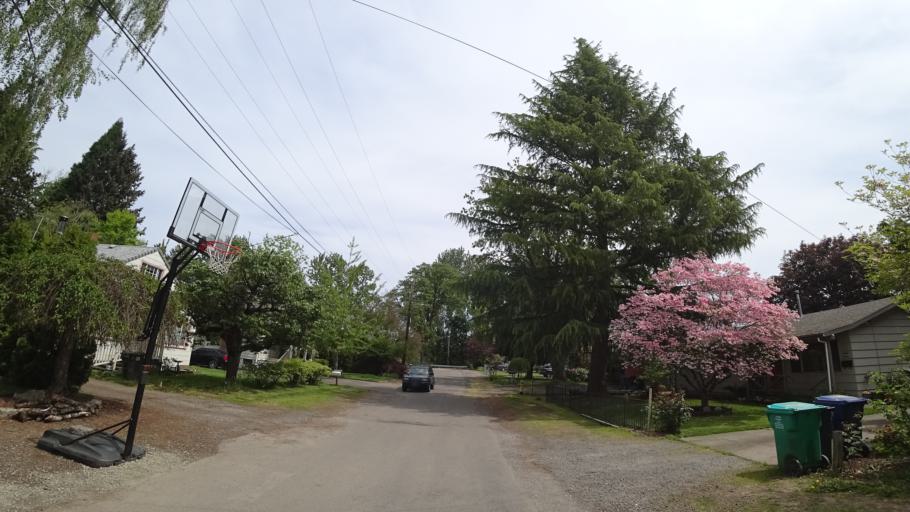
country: US
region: Oregon
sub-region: Clackamas County
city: Milwaukie
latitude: 45.4587
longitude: -122.6171
